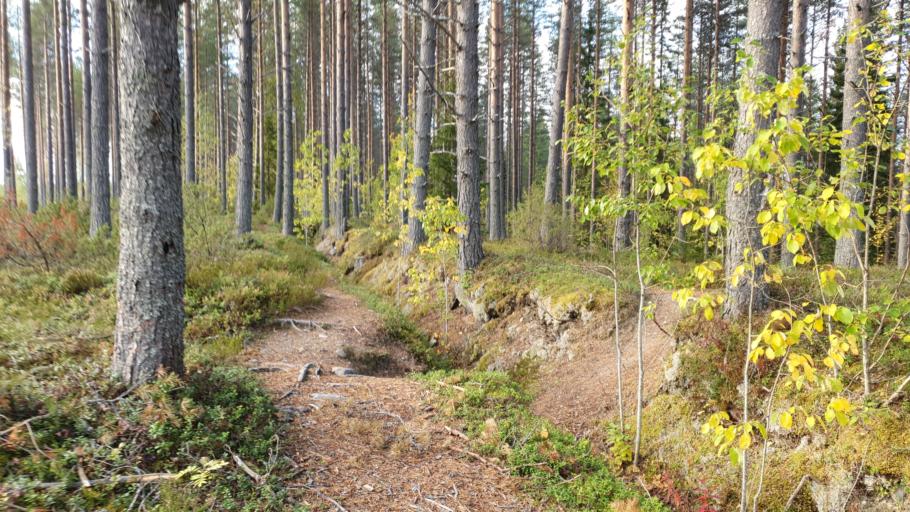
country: FI
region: Kainuu
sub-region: Kehys-Kainuu
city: Kuhmo
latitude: 63.9319
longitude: 29.9709
